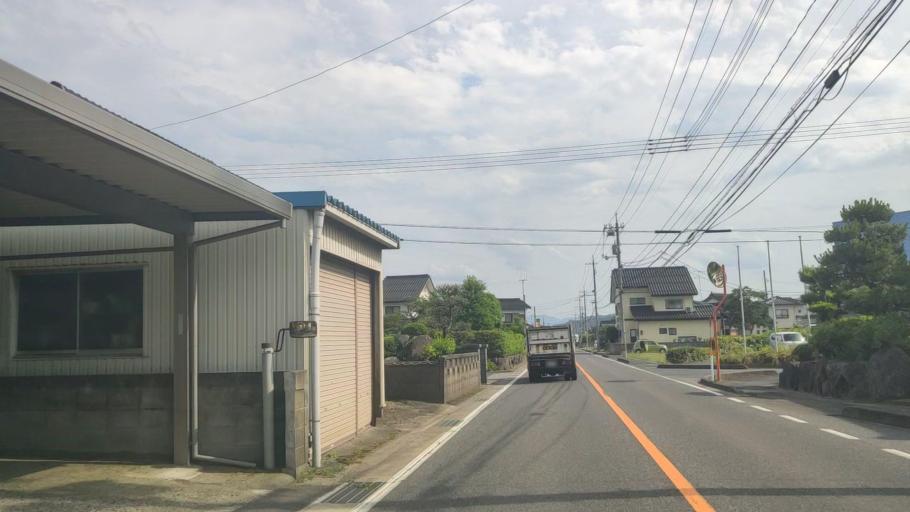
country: JP
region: Tottori
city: Tottori
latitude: 35.4688
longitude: 134.2040
